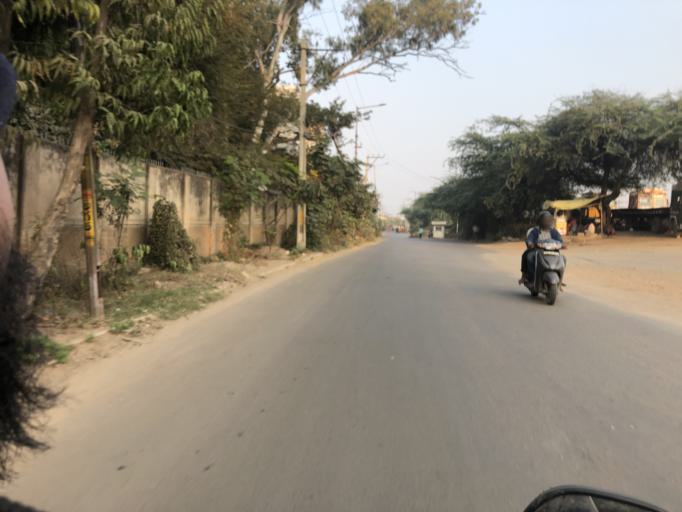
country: IN
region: Telangana
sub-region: Rangareddi
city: Kukatpalli
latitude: 17.4624
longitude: 78.4397
